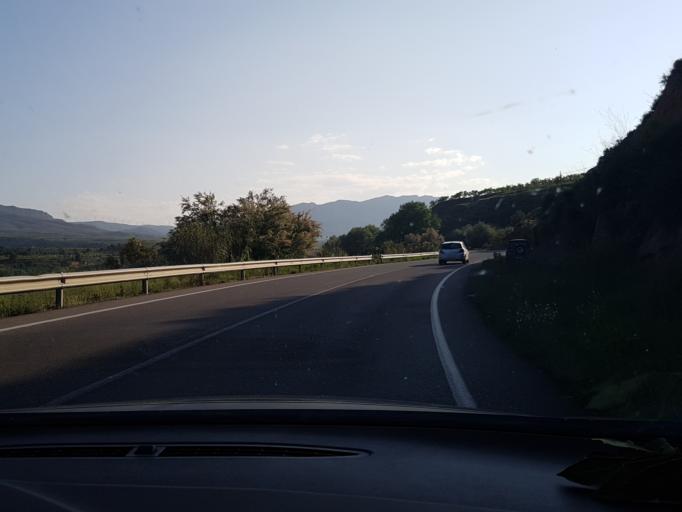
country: ES
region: La Rioja
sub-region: Provincia de La Rioja
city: Arnedo
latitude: 42.2172
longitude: -2.1221
